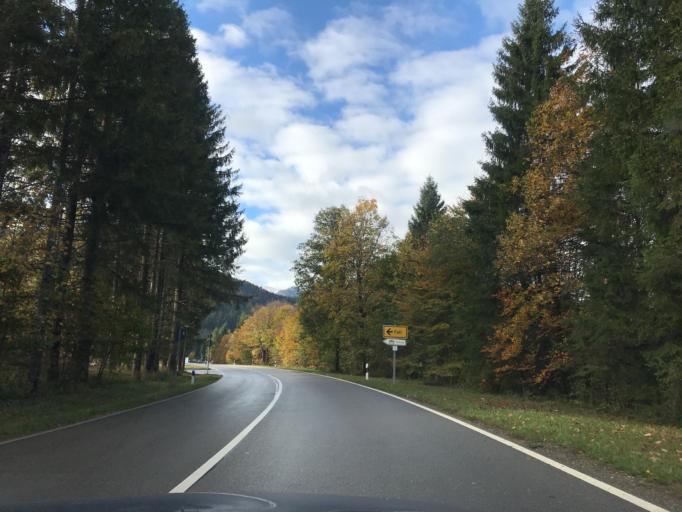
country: DE
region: Bavaria
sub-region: Upper Bavaria
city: Jachenau
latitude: 47.5714
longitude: 11.5313
